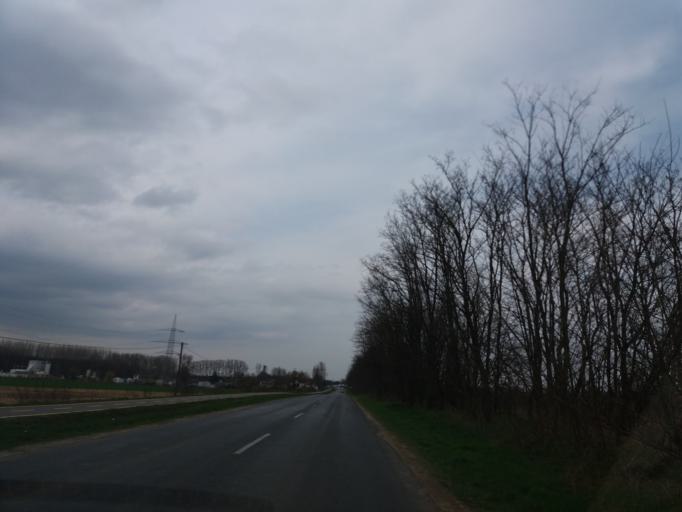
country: HU
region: Szabolcs-Szatmar-Bereg
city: Anarcs
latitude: 48.1936
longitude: 22.0979
